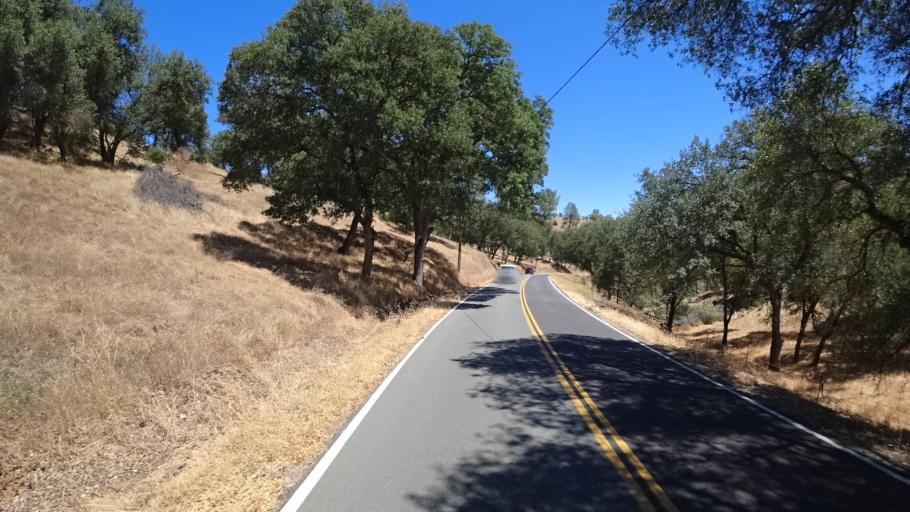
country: US
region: California
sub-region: Calaveras County
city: San Andreas
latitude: 38.1578
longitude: -120.6692
